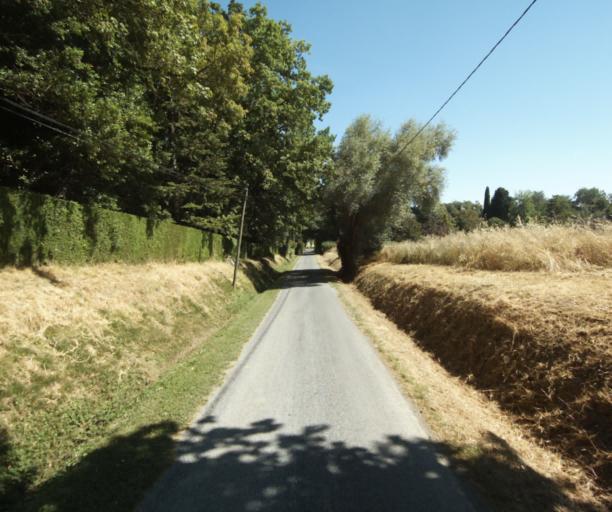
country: FR
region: Midi-Pyrenees
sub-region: Departement de la Haute-Garonne
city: Saint-Felix-Lauragais
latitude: 43.4960
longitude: 1.9398
